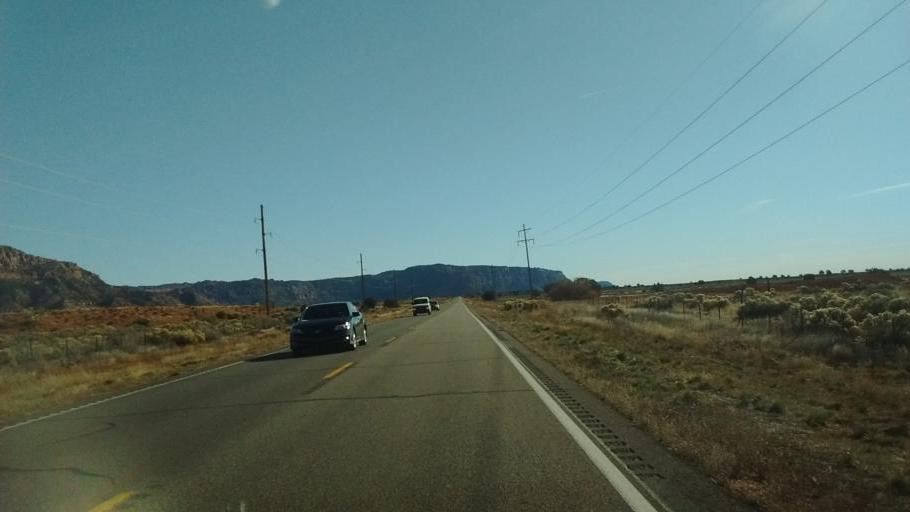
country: US
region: Arizona
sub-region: Mohave County
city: Colorado City
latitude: 37.0152
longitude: -113.0250
